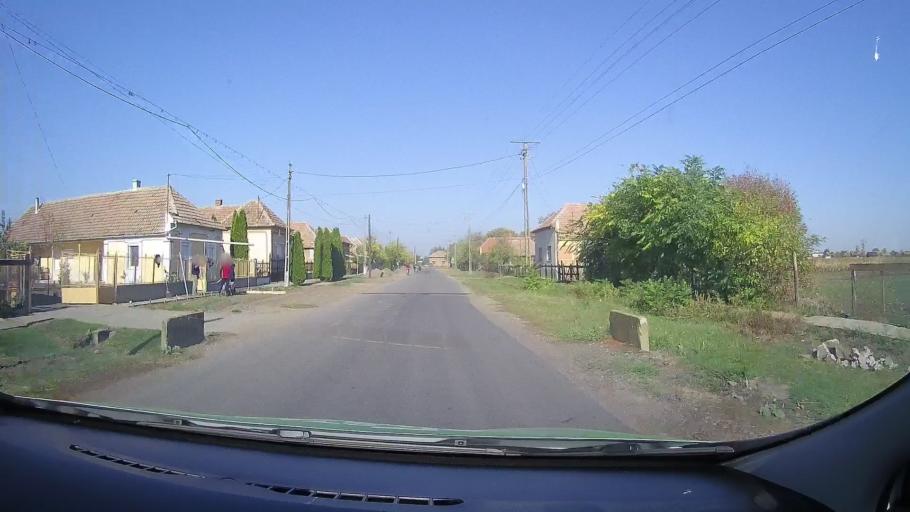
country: RO
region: Satu Mare
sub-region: Comuna Ciumesti
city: Ciumesti
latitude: 47.6545
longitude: 22.3347
